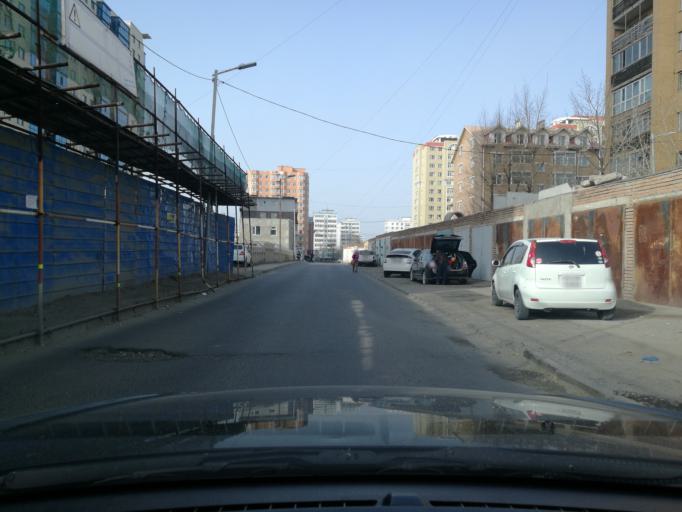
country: MN
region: Ulaanbaatar
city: Ulaanbaatar
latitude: 47.9104
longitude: 106.9072
